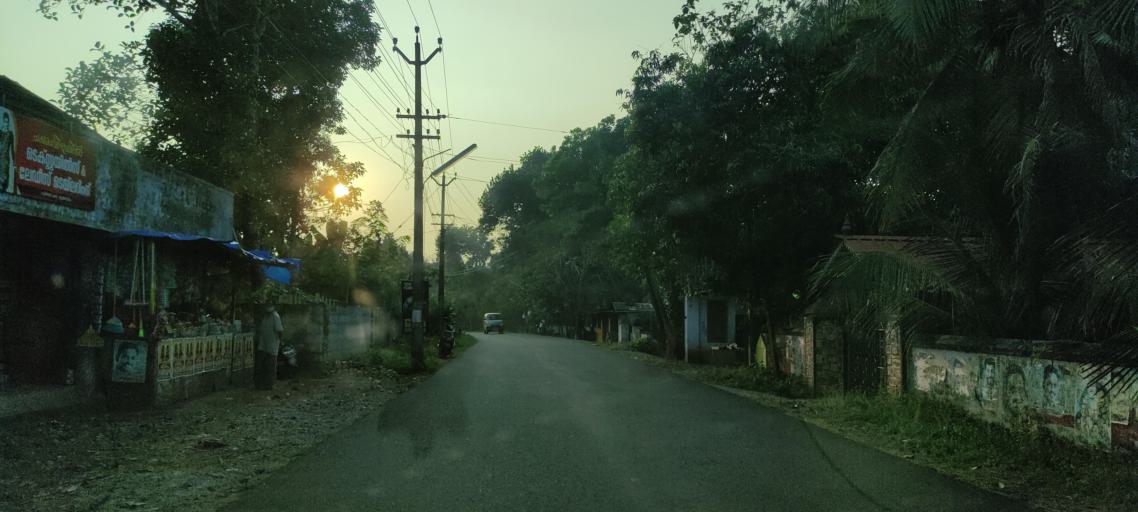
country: IN
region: Kerala
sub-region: Alappuzha
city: Kattanam
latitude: 9.1453
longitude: 76.5734
